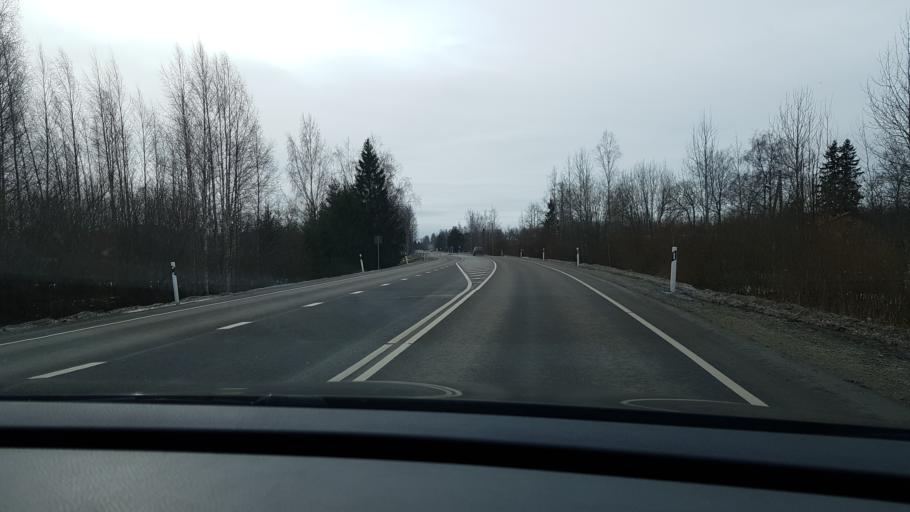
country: EE
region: Paernumaa
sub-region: Sindi linn
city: Sindi
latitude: 58.4006
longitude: 24.6513
